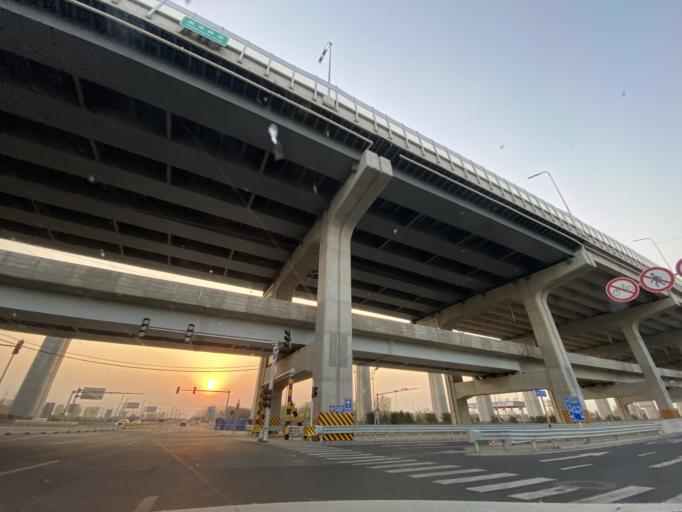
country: CN
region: Beijing
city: Weishanzhuang
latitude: 39.6146
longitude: 116.3789
